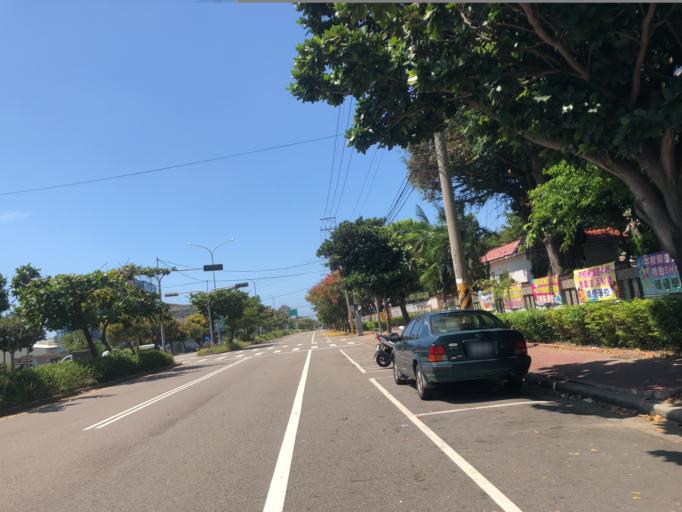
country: TW
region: Taiwan
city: Fengyuan
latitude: 24.2785
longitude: 120.5577
